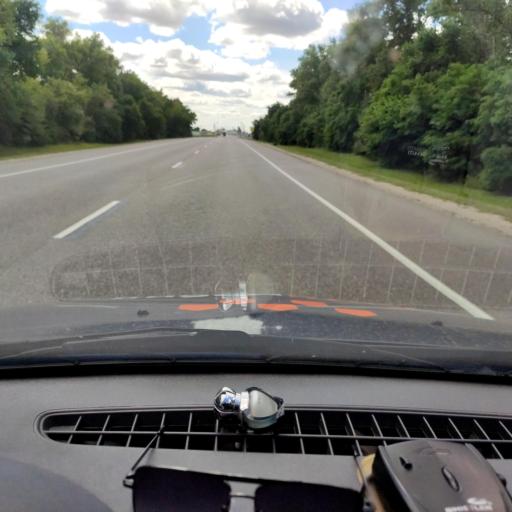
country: RU
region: Lipetsk
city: Khlevnoye
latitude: 52.2722
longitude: 39.1684
